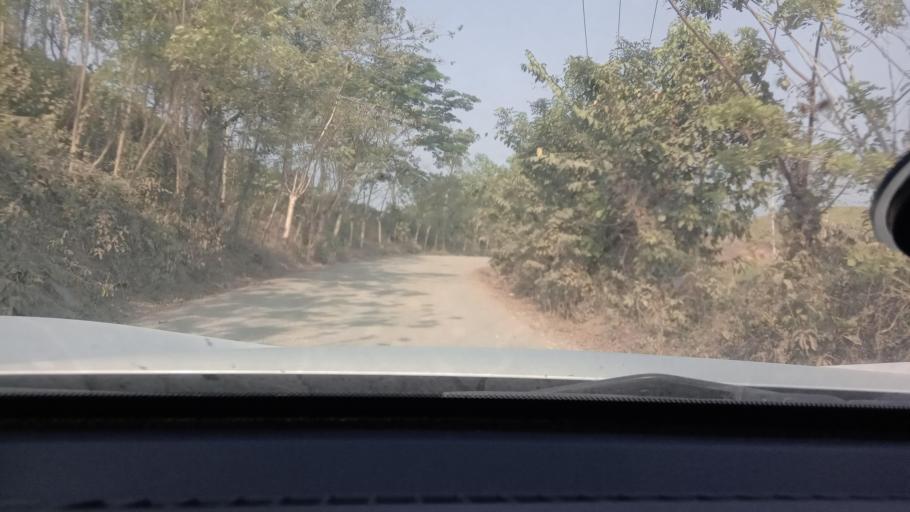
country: MX
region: Tabasco
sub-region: Huimanguillo
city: Francisco Rueda
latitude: 17.6540
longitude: -93.8950
